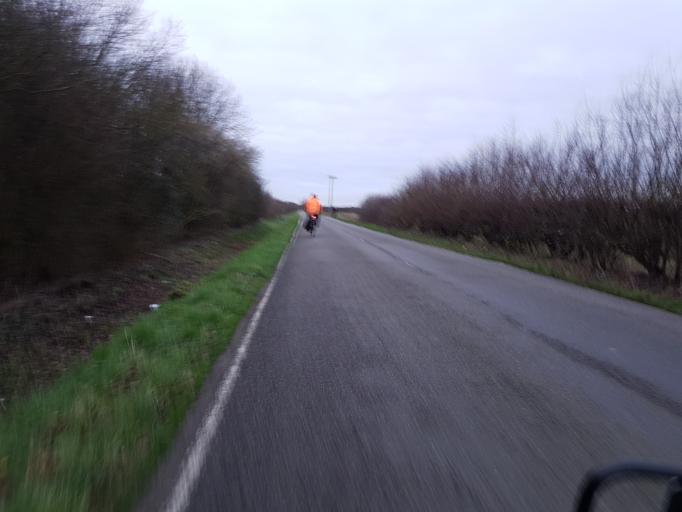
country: GB
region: England
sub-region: Cambridgeshire
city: Fulbourn
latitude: 52.2133
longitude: 0.2014
